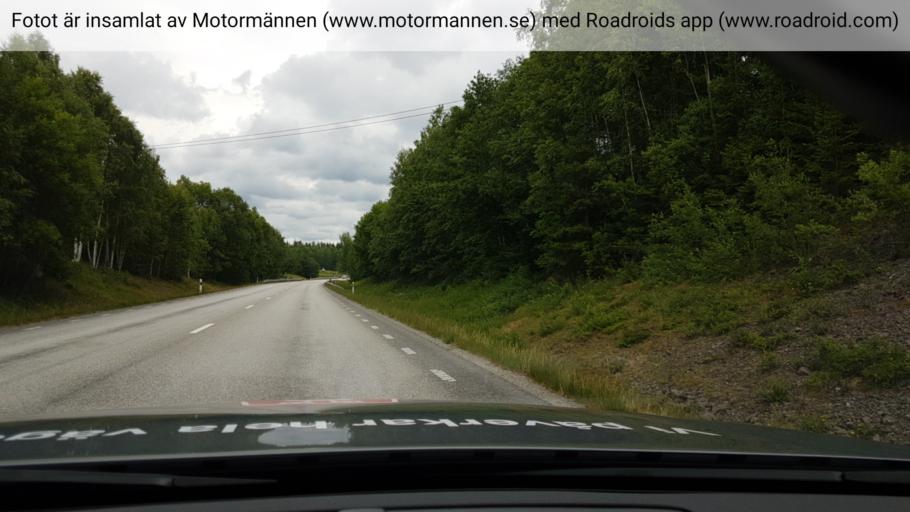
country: SE
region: OErebro
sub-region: Lindesbergs Kommun
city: Lindesberg
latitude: 59.6426
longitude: 15.2311
